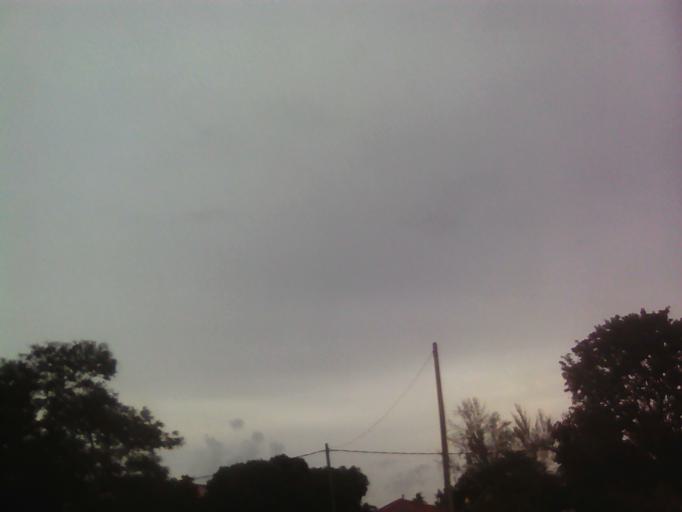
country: MY
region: Penang
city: Perai
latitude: 5.3991
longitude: 100.4092
